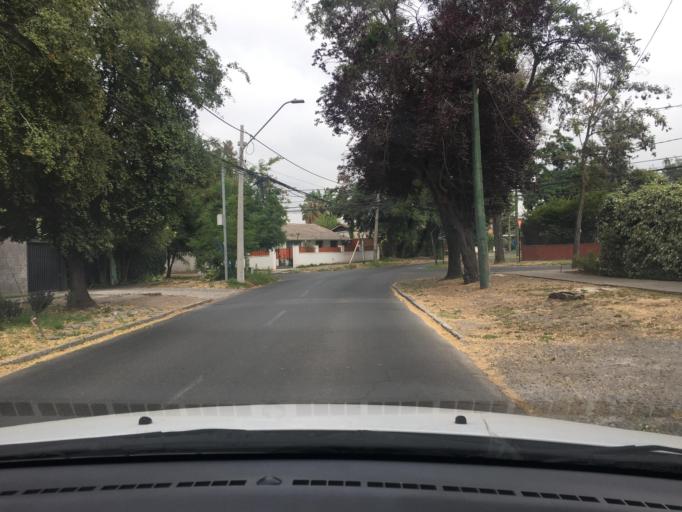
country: CL
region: Santiago Metropolitan
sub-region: Provincia de Santiago
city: Villa Presidente Frei, Nunoa, Santiago, Chile
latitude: -33.4482
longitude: -70.5604
